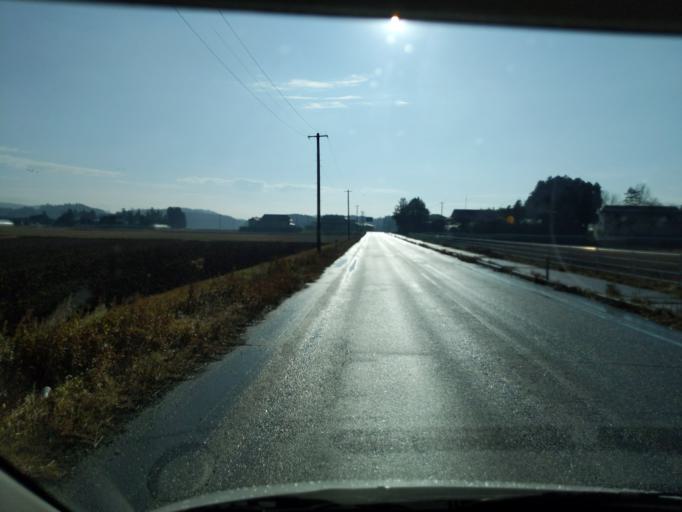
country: JP
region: Iwate
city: Ichinoseki
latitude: 38.7707
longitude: 141.1796
